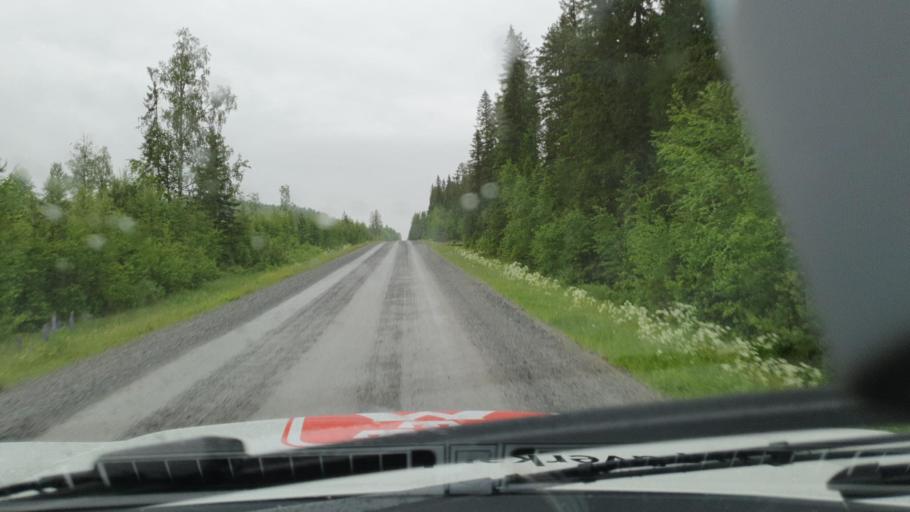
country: SE
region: Vaesterbotten
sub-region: Bjurholms Kommun
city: Bjurholm
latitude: 63.8502
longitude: 19.4757
